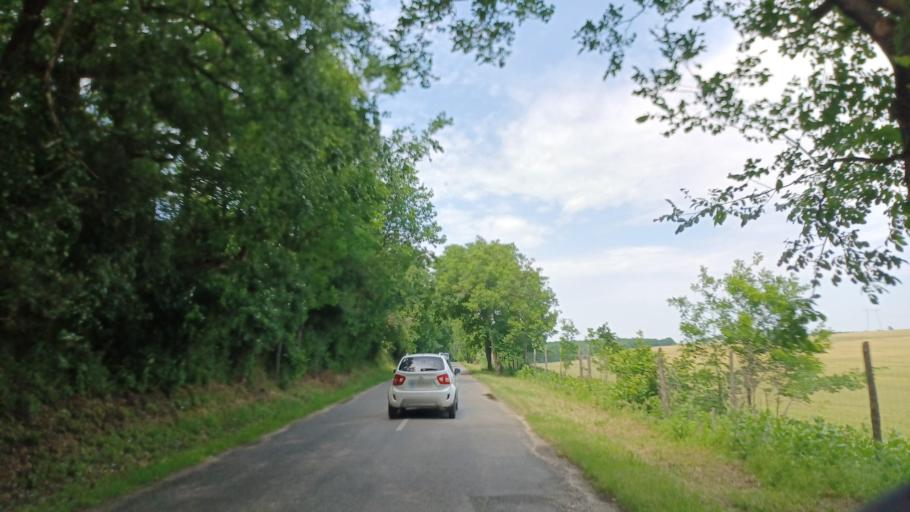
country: HU
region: Tolna
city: Simontornya
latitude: 46.7088
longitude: 18.5090
